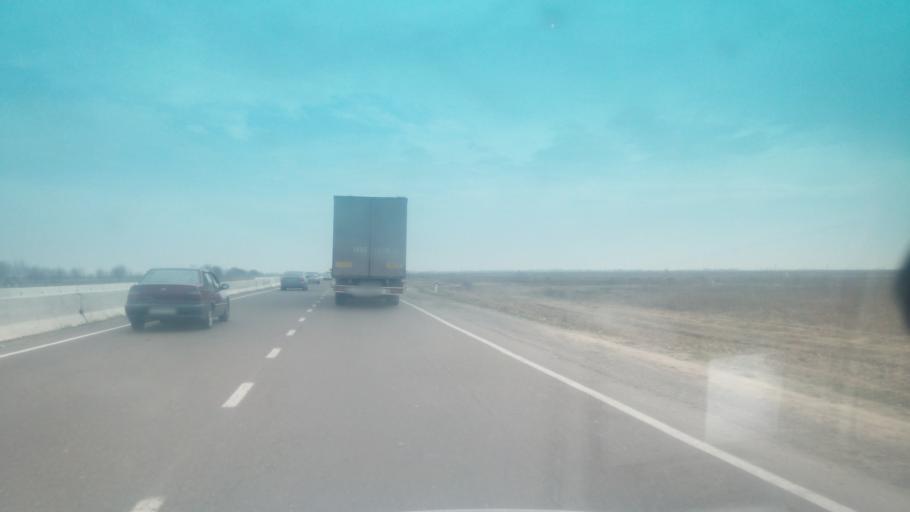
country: KZ
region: Ongtustik Qazaqstan
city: Myrzakent
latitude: 40.5153
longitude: 68.4830
